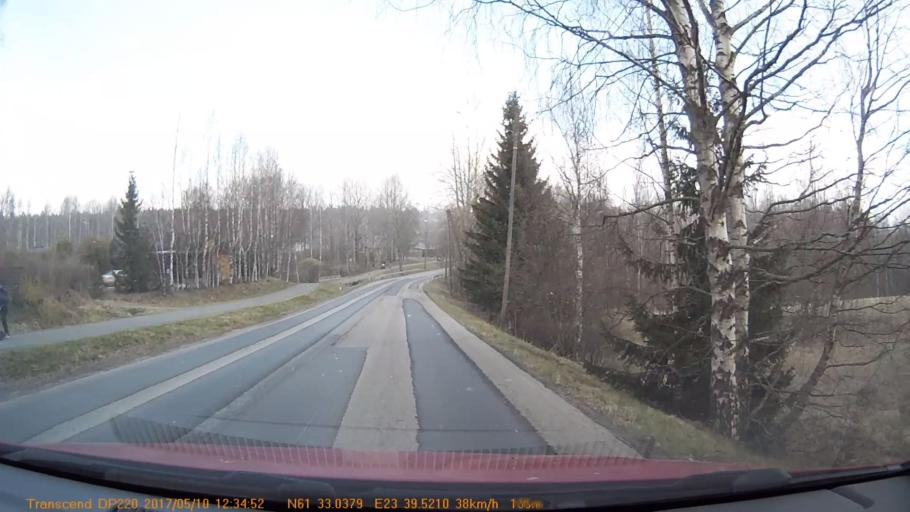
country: FI
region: Pirkanmaa
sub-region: Tampere
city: Yloejaervi
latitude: 61.5506
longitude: 23.6589
